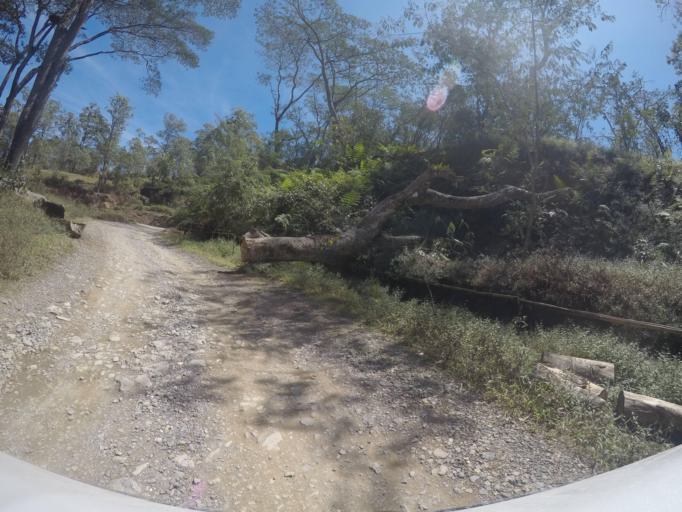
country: TL
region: Ermera
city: Gleno
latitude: -8.7858
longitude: 125.3784
